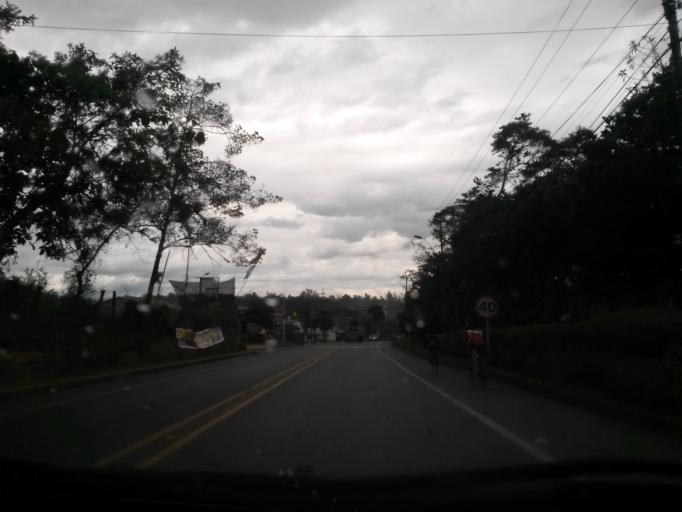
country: CO
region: Cauca
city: Popayan
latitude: 2.5065
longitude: -76.5498
